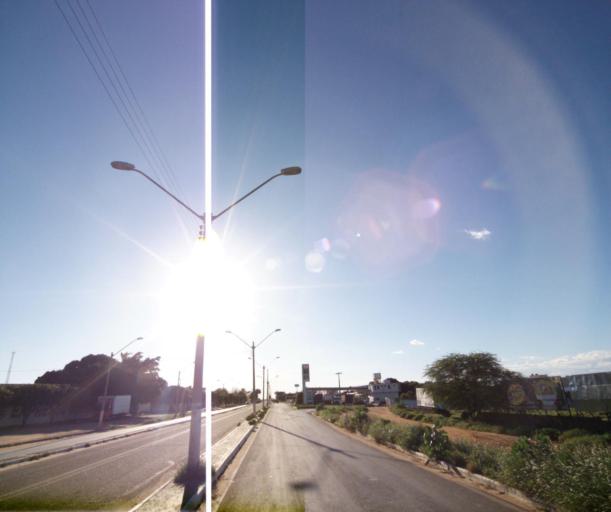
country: BR
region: Bahia
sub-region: Guanambi
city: Guanambi
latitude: -14.2105
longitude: -42.7887
